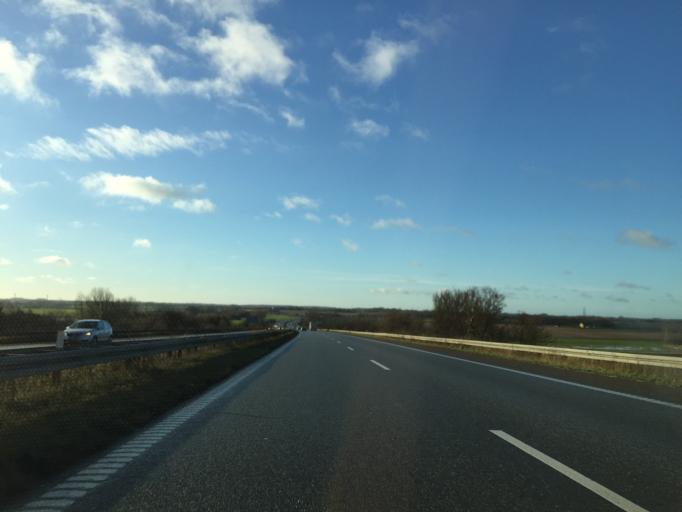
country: DK
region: Zealand
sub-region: Slagelse Kommune
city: Forlev
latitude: 55.3750
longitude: 11.3061
